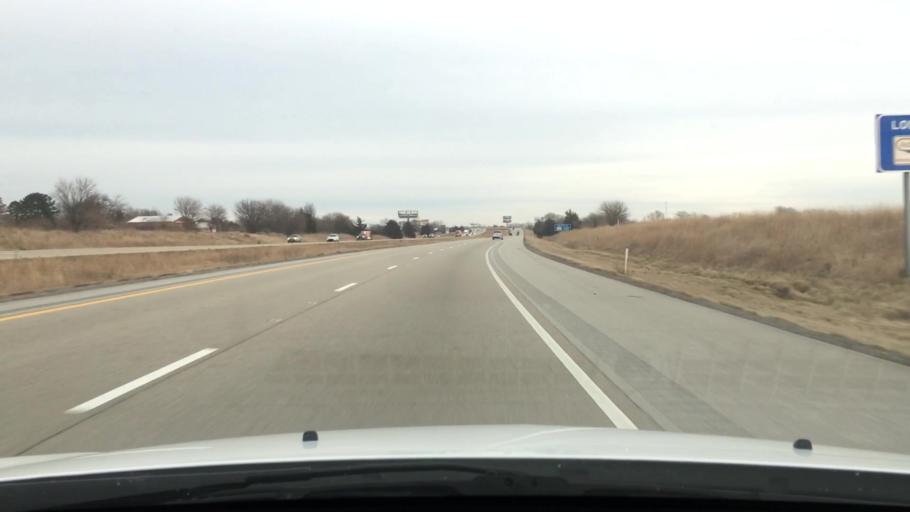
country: US
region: Illinois
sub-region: Logan County
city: Atlanta
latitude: 40.2493
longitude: -89.2410
